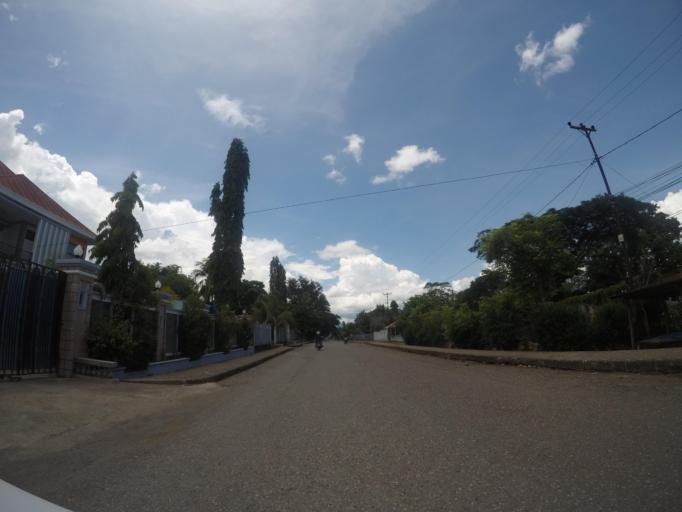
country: TL
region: Bobonaro
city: Maliana
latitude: -8.9900
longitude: 125.2018
